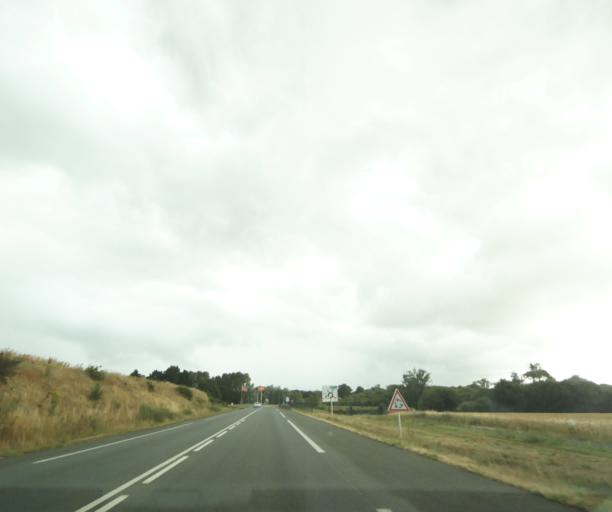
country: FR
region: Pays de la Loire
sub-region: Departement de la Vendee
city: Saint-Hilaire-de-Talmont
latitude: 46.4639
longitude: -1.6018
